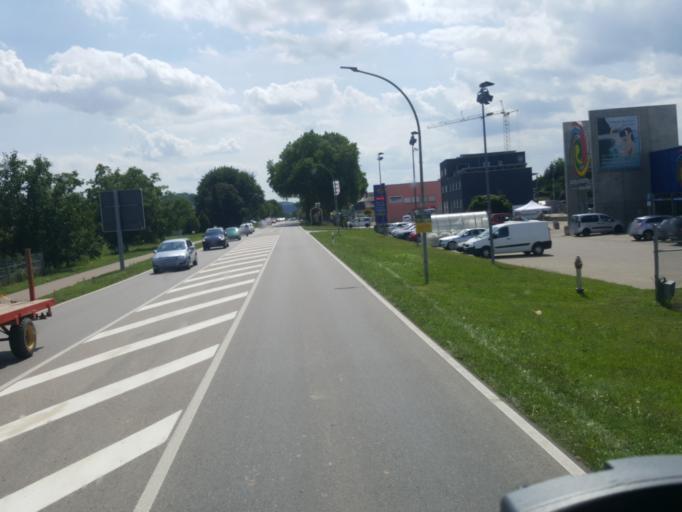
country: DE
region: Baden-Wuerttemberg
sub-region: Freiburg Region
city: Auggen
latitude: 47.7909
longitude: 7.5919
